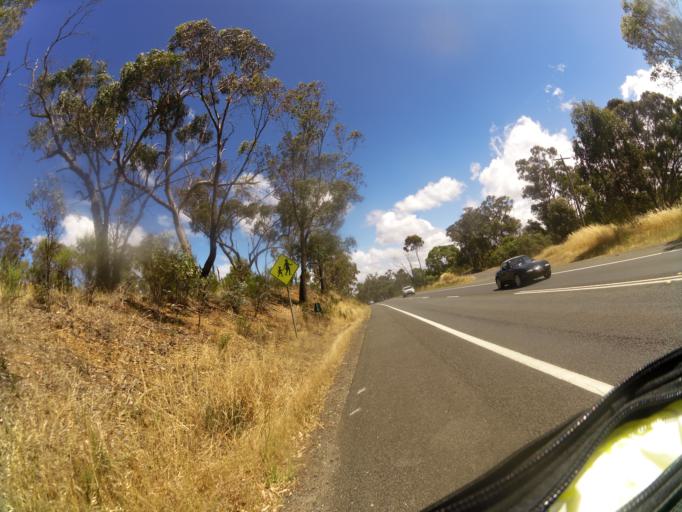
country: AU
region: Victoria
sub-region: Mount Alexander
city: Castlemaine
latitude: -37.0209
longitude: 144.2387
